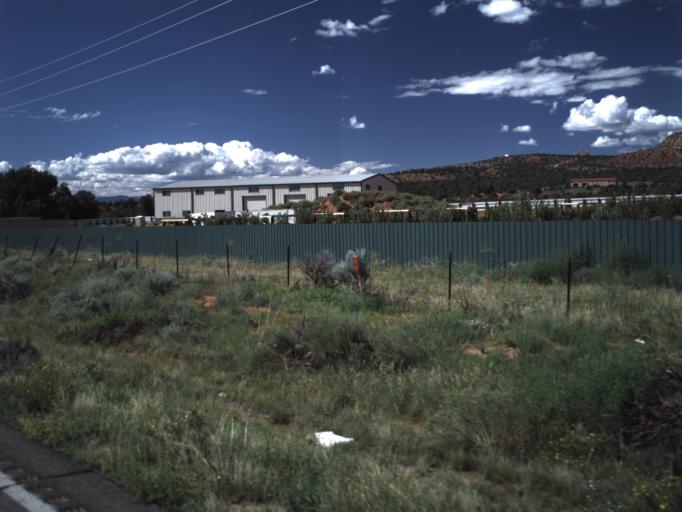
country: US
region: Arizona
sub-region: Mohave County
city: Colorado City
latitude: 37.0368
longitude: -113.0690
